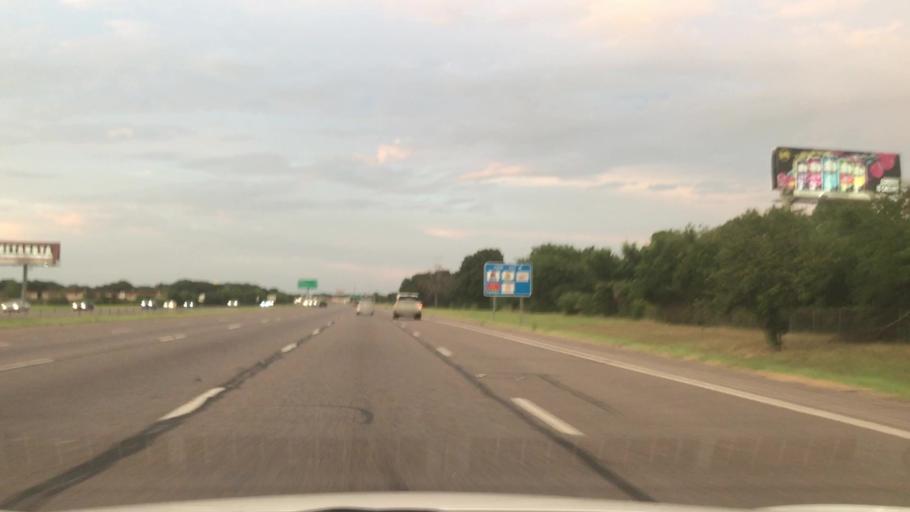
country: US
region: Texas
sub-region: Dallas County
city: Balch Springs
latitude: 32.7098
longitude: -96.6210
